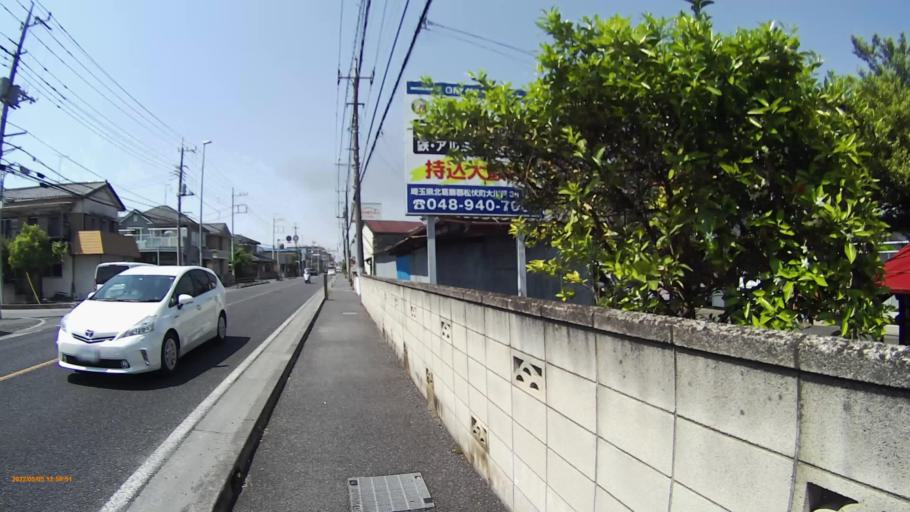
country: JP
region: Saitama
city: Kasukabe
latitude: 35.9613
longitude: 139.7729
